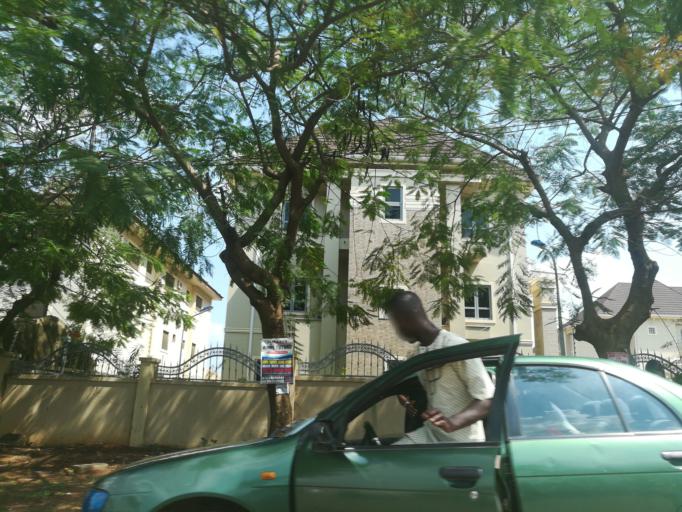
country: NG
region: Abuja Federal Capital Territory
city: Abuja
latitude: 9.0521
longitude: 7.4463
